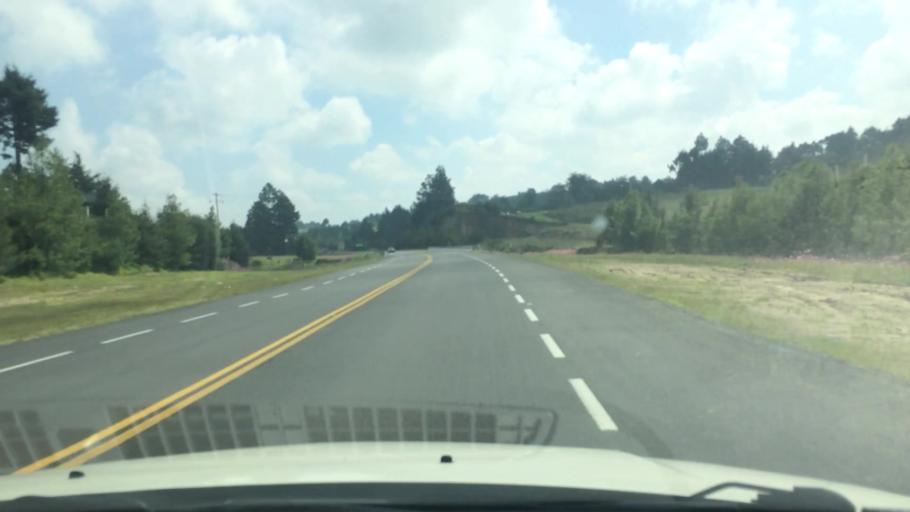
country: MX
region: Mexico
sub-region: Villa Victoria
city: Colonia Doctor Gustavo Baz
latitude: 19.3577
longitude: -99.9597
